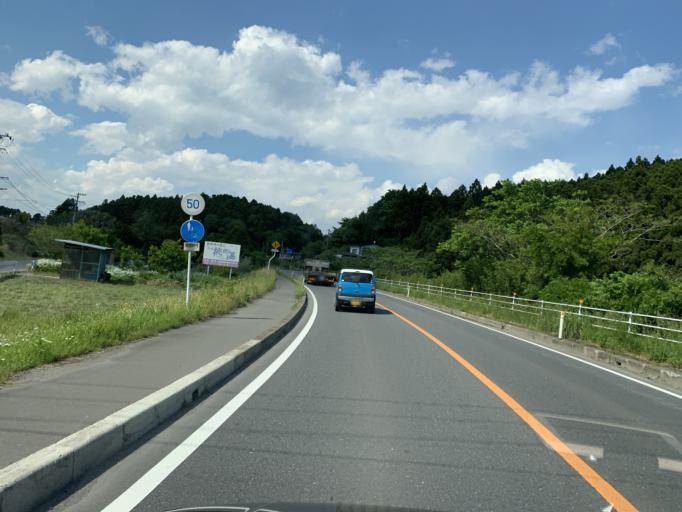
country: JP
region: Miyagi
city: Wakuya
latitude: 38.4937
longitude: 141.1143
